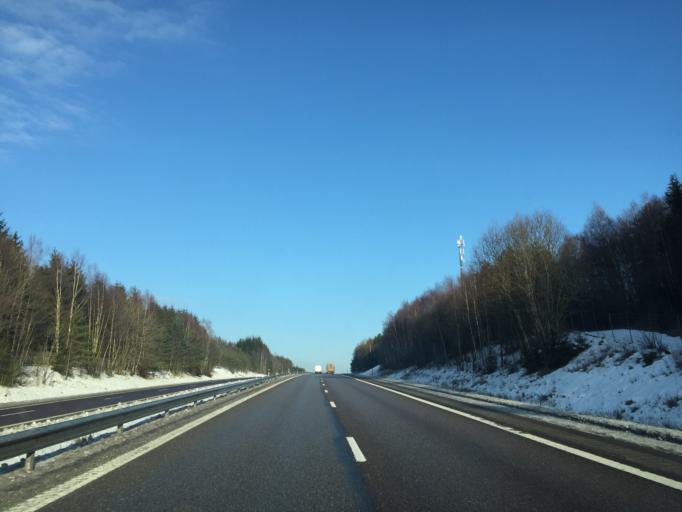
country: SE
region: Vaestra Goetaland
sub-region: Stenungsunds Kommun
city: Stenungsund
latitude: 58.0791
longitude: 11.8871
